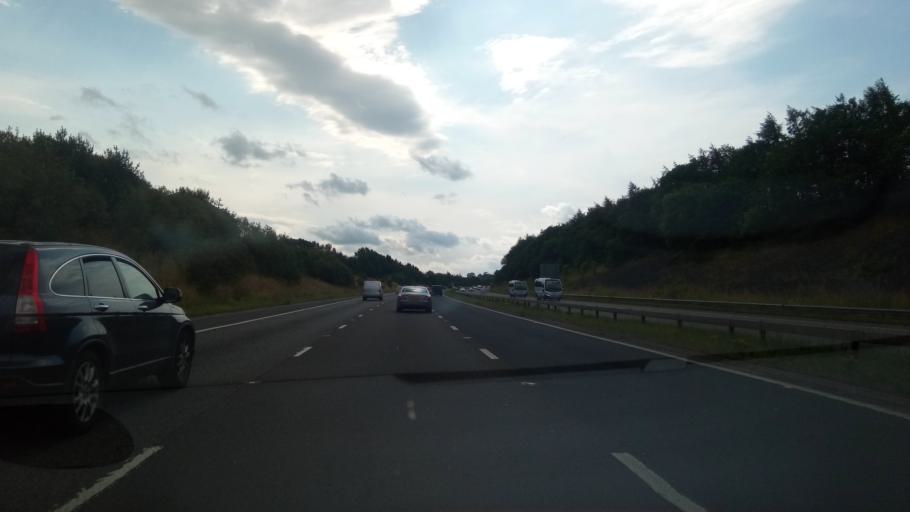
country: GB
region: England
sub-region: Cumbria
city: Penrith
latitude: 54.6460
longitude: -2.7432
